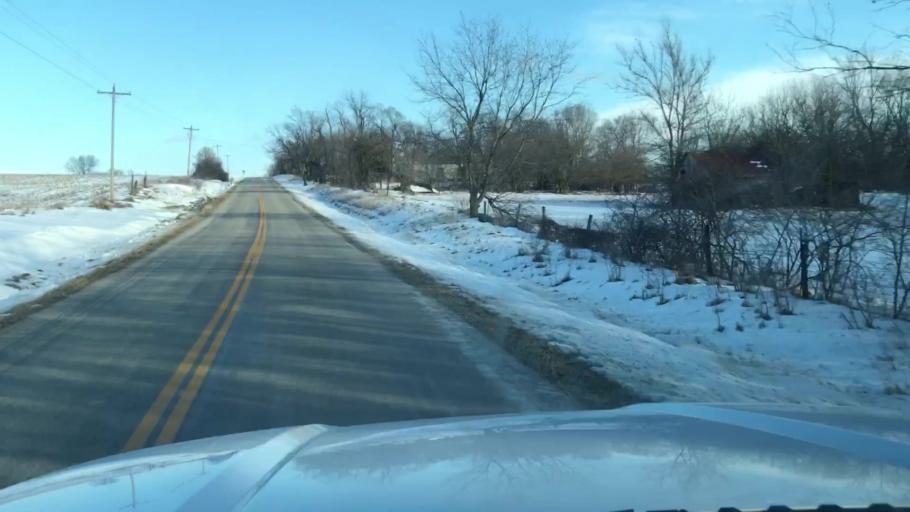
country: US
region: Missouri
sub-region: Holt County
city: Oregon
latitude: 40.1009
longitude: -95.0194
